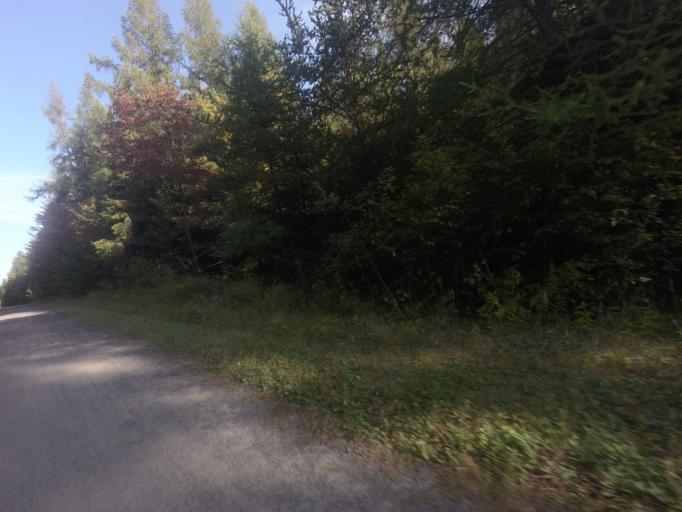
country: CA
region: Quebec
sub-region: Laurentides
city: Val-David
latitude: 46.0209
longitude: -74.1913
